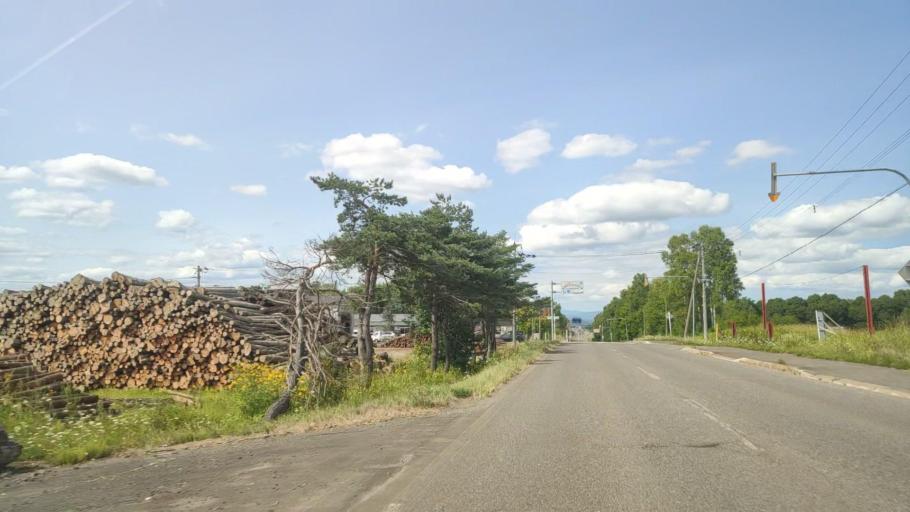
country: JP
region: Hokkaido
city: Nayoro
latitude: 44.2844
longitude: 142.4295
